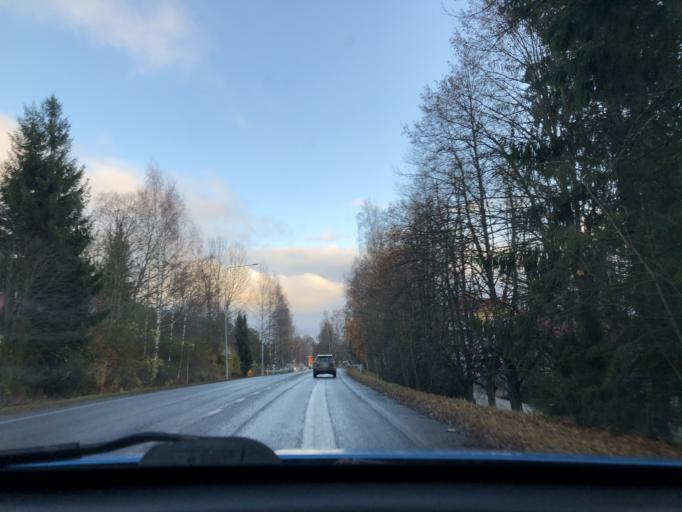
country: FI
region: Pirkanmaa
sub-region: Tampere
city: Kangasala
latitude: 61.4667
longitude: 24.0520
